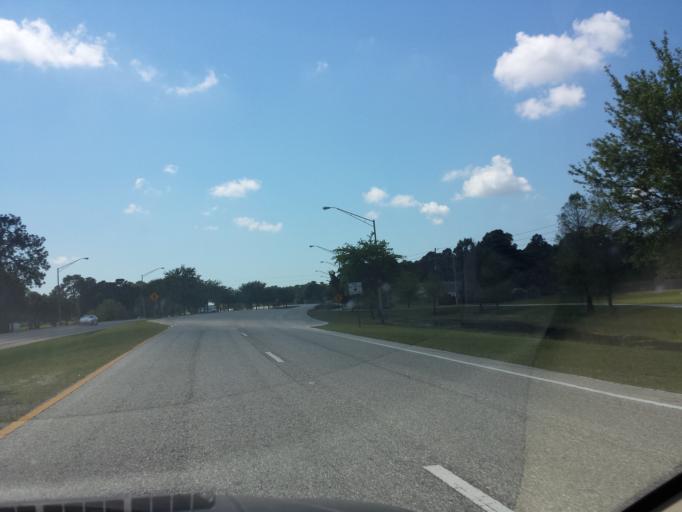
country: US
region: Florida
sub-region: Sarasota County
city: North Port
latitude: 27.0899
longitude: -82.2084
